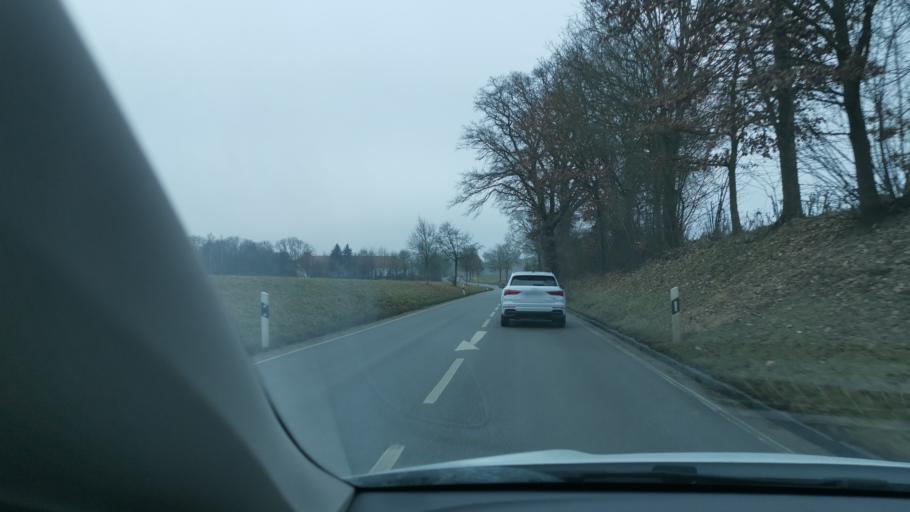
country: DE
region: Bavaria
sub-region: Swabia
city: Thierhaupten
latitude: 48.5566
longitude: 10.9093
